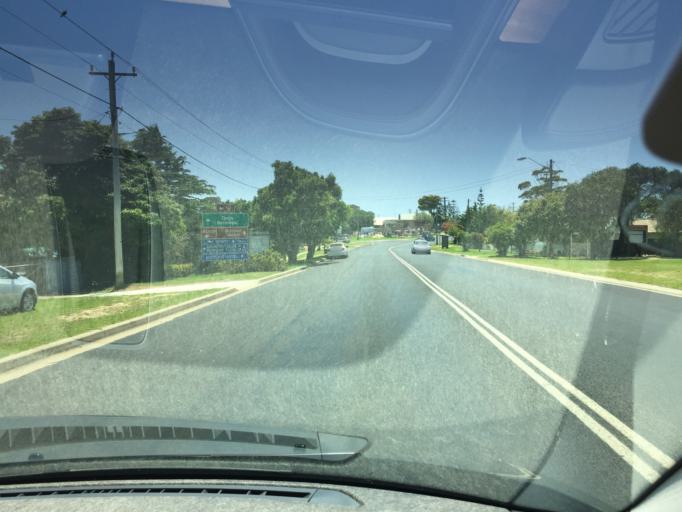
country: AU
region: New South Wales
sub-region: Bega Valley
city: Bega
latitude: -36.7308
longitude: 149.9845
